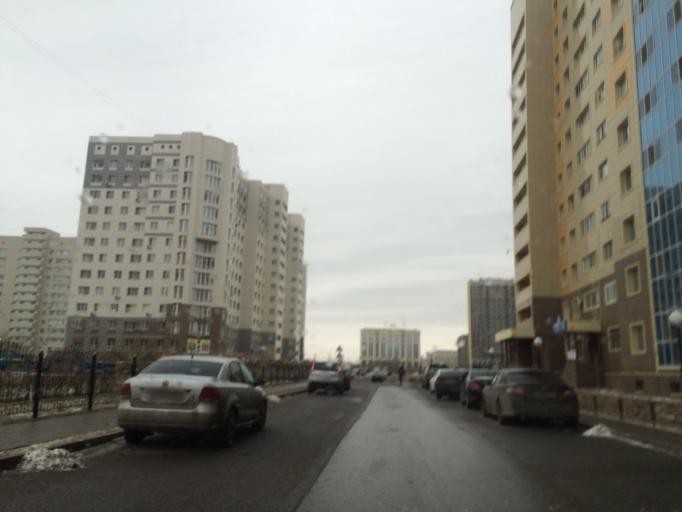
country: KZ
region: Astana Qalasy
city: Astana
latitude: 51.1221
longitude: 71.4180
